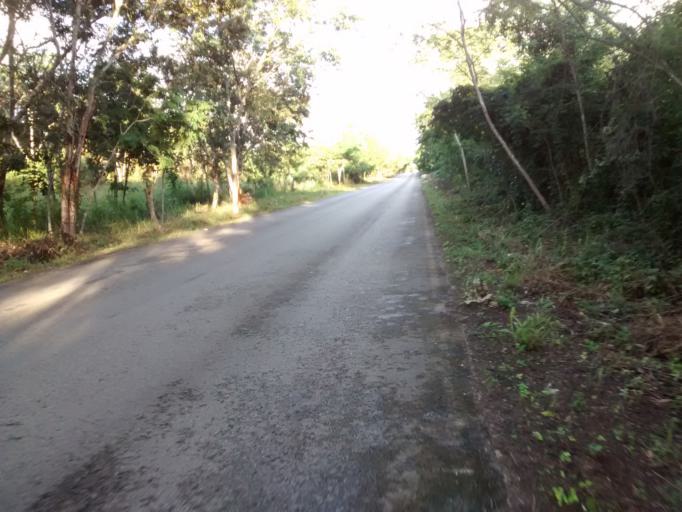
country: MX
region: Yucatan
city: Valladolid
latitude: 20.7312
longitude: -88.2199
